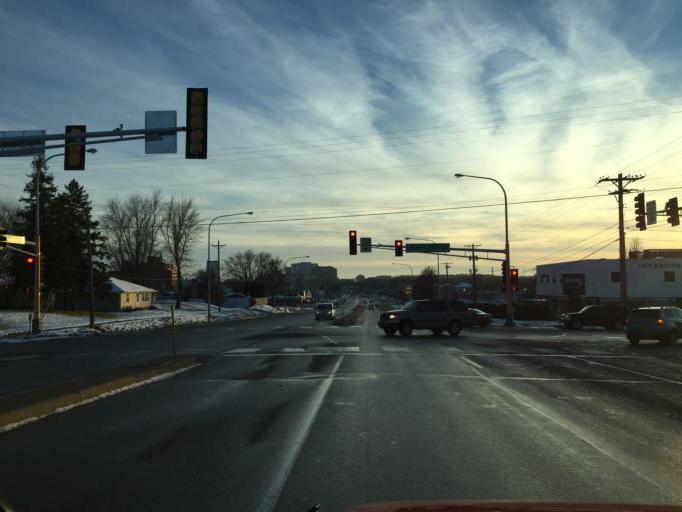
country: US
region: Minnesota
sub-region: Olmsted County
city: Rochester
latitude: 44.0417
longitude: -92.4607
